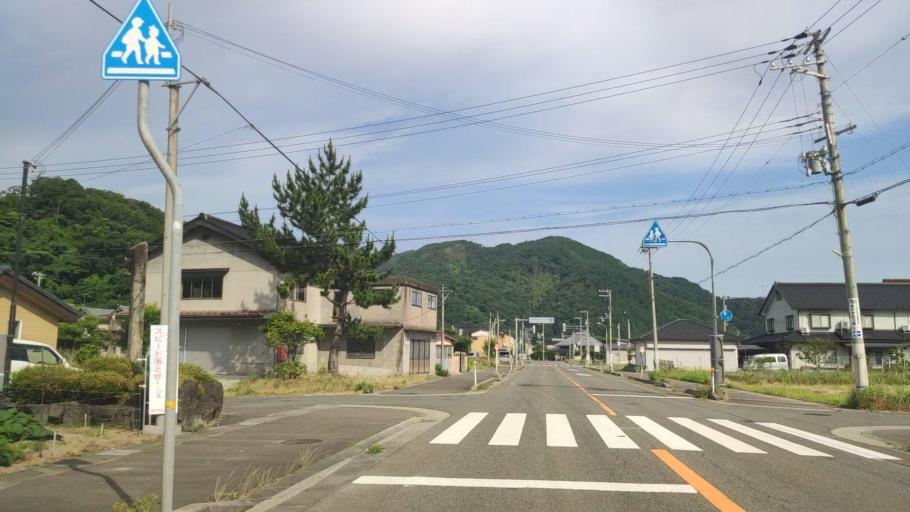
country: JP
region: Hyogo
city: Toyooka
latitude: 35.6417
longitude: 134.8340
